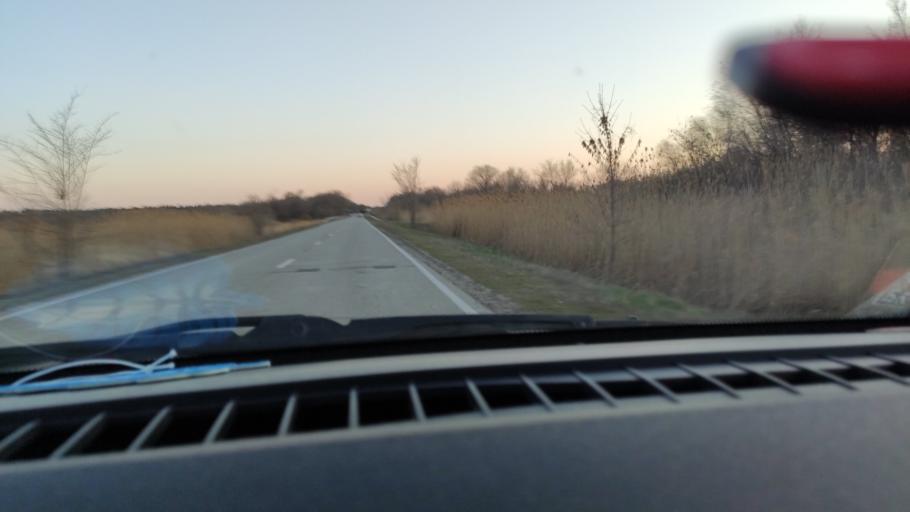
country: RU
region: Saratov
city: Privolzhskiy
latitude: 51.2484
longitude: 45.9371
